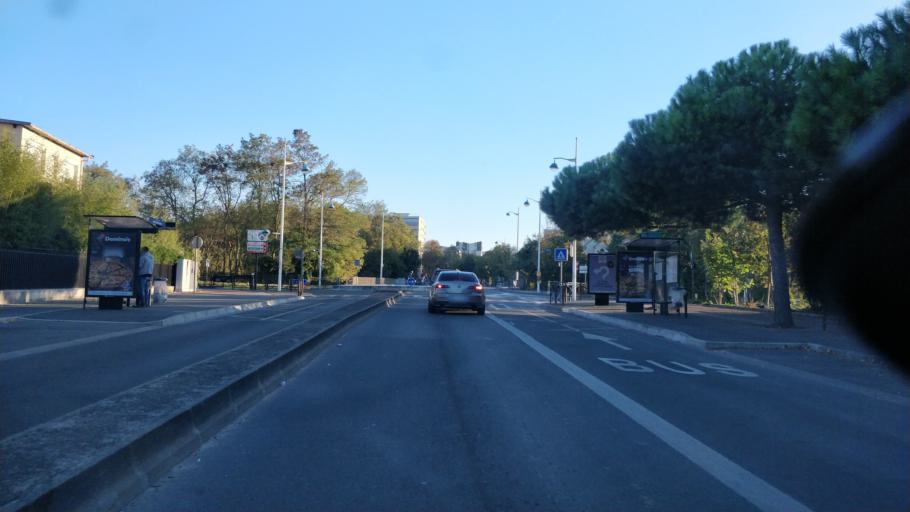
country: FR
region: Ile-de-France
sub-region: Departement de Seine-Saint-Denis
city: Gournay-sur-Marne
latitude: 48.8507
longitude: 2.5851
